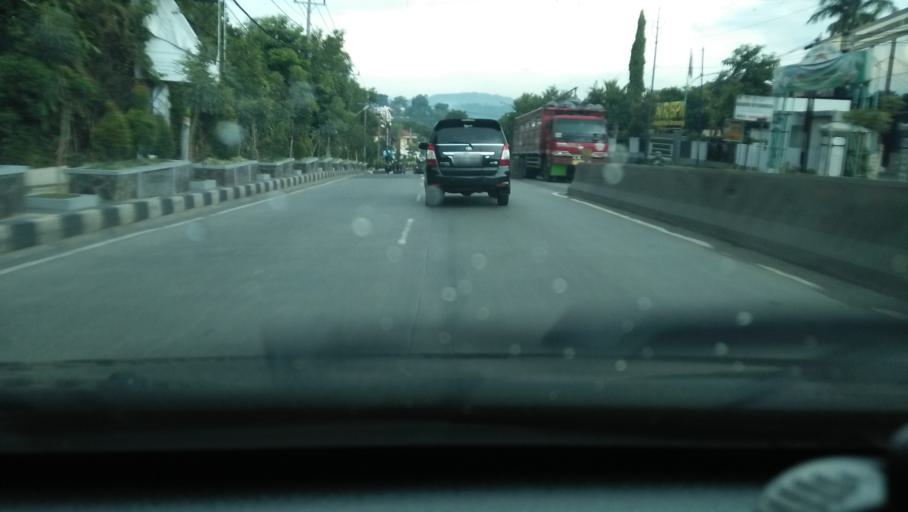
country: ID
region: Central Java
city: Ungaran
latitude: -7.1127
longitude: 110.4125
